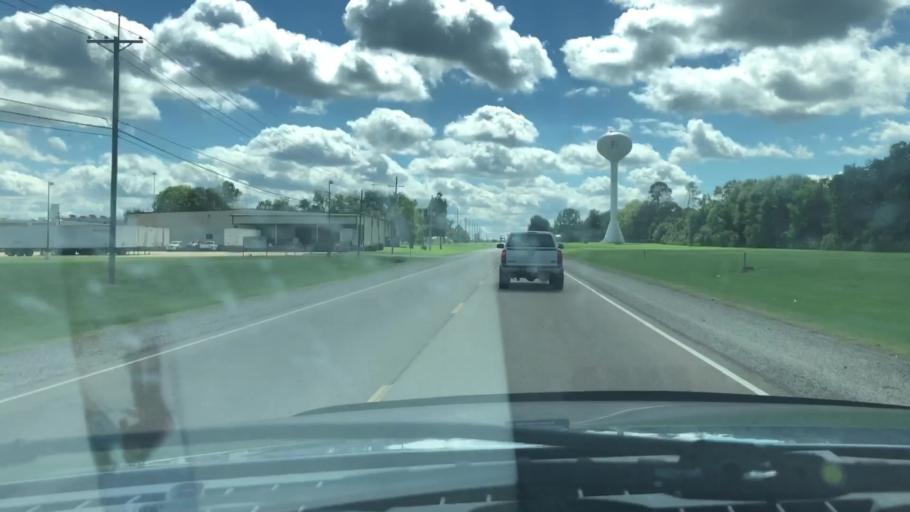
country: US
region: Texas
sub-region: Bowie County
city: Wake Village
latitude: 33.3809
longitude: -94.0921
